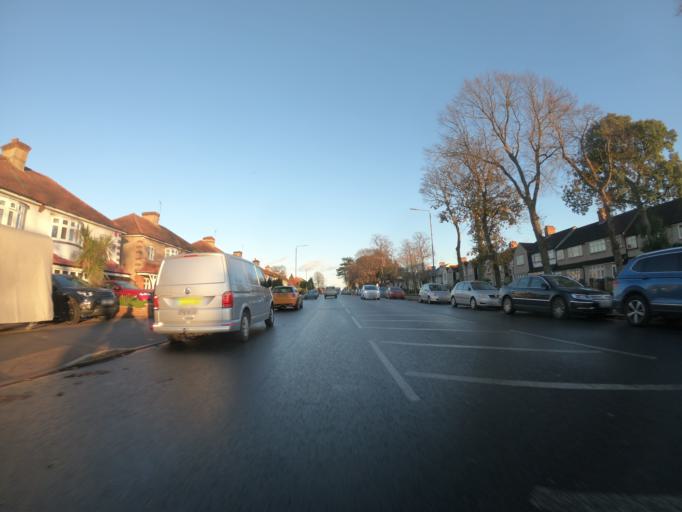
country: GB
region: England
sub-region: Greater London
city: Abbey Wood
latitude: 51.4814
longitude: 0.1279
